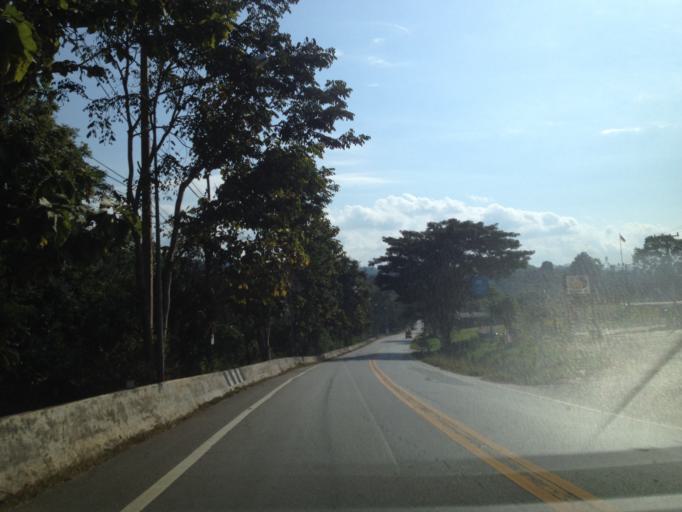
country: TH
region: Mae Hong Son
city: Ban Huai I Huak
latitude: 18.1518
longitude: 98.2445
